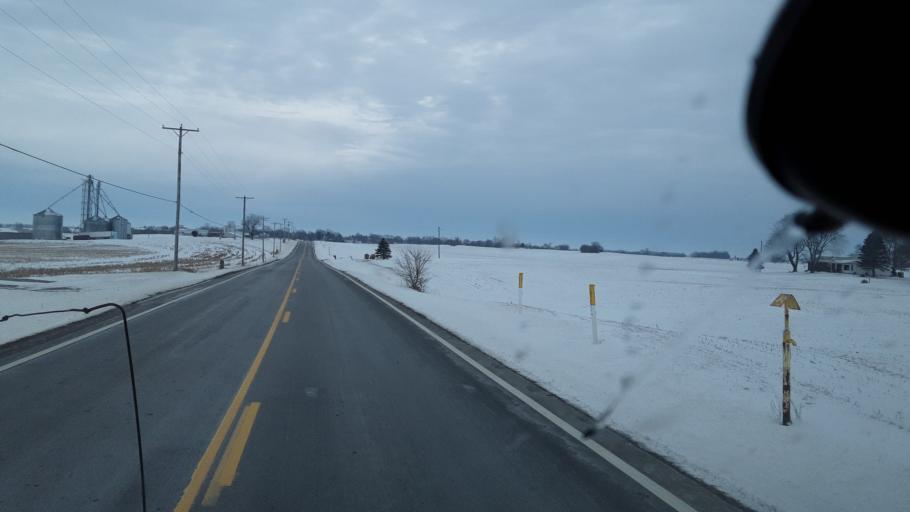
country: US
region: Ohio
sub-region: Madison County
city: Bethel
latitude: 39.7469
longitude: -83.4809
